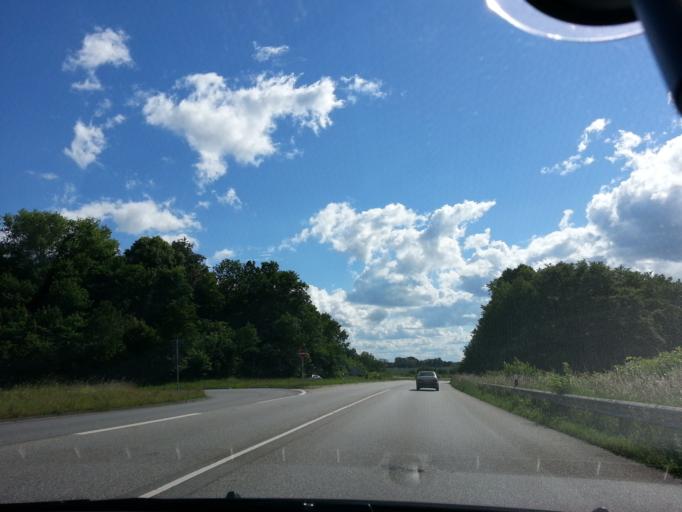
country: DE
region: Schleswig-Holstein
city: Alt Molln
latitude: 53.6218
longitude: 10.6647
